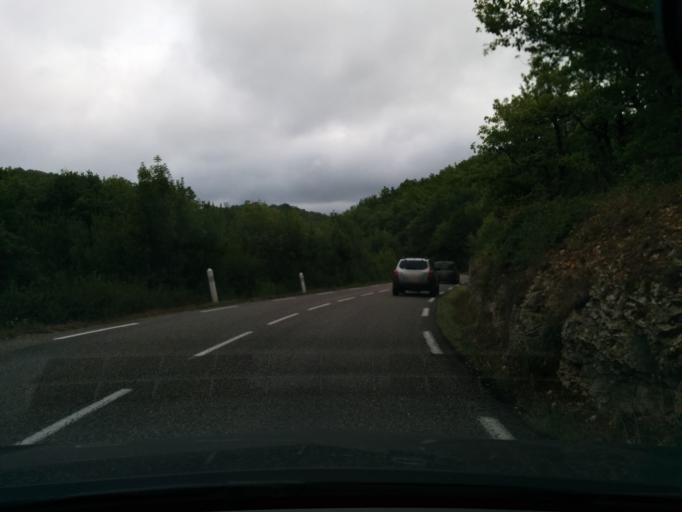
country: FR
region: Midi-Pyrenees
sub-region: Departement du Lot
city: Cahors
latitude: 44.3982
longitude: 1.3699
